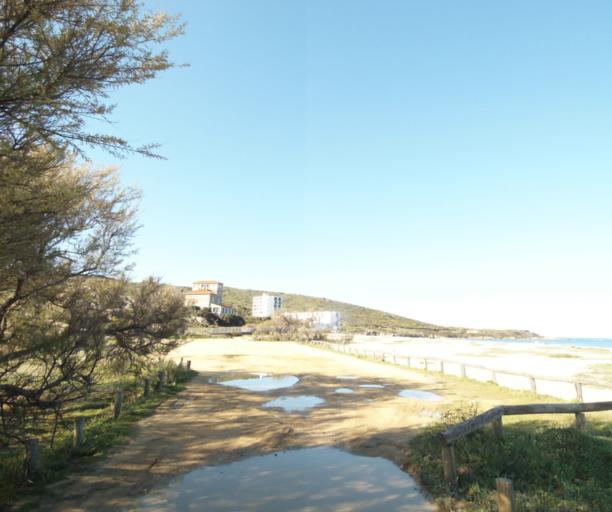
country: FR
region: Corsica
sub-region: Departement de la Corse-du-Sud
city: Propriano
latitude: 41.6741
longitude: 8.8934
